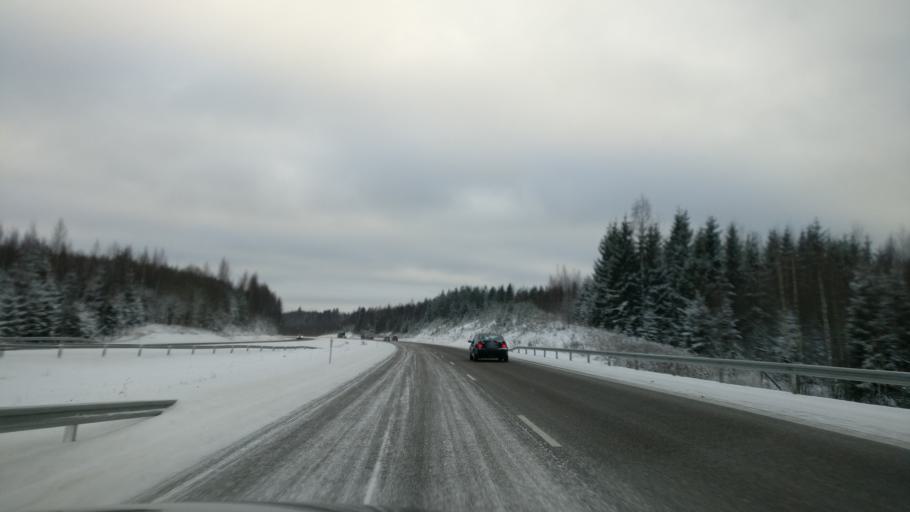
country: FI
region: Paijanne Tavastia
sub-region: Lahti
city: Nastola
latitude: 61.0288
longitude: 25.8346
